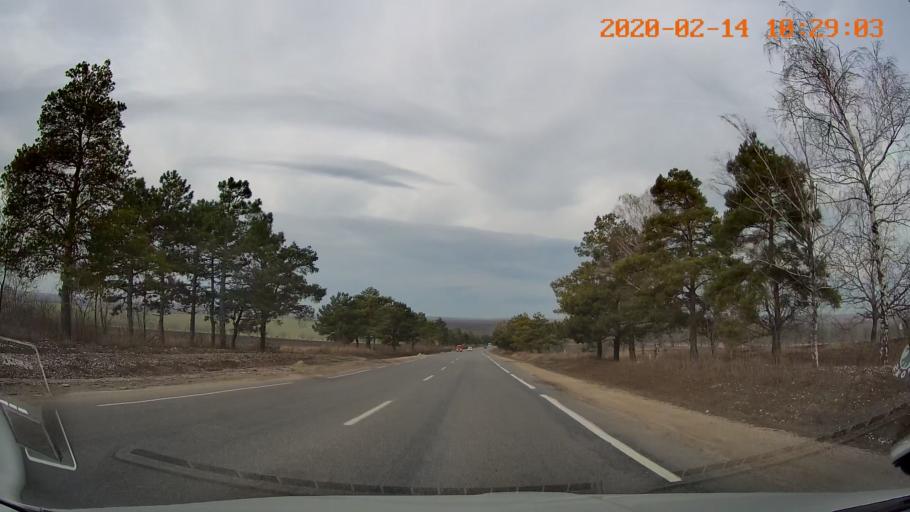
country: MD
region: Drochia
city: Drochia
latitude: 47.8647
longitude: 27.7441
